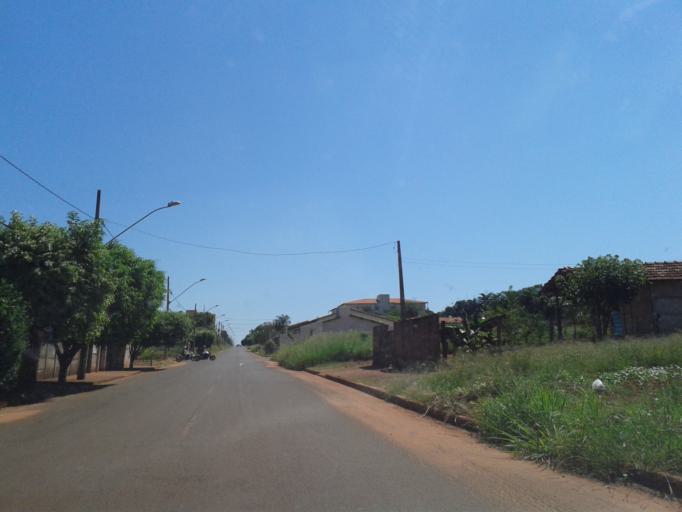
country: BR
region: Minas Gerais
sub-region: Ituiutaba
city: Ituiutaba
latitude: -18.9987
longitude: -49.4549
